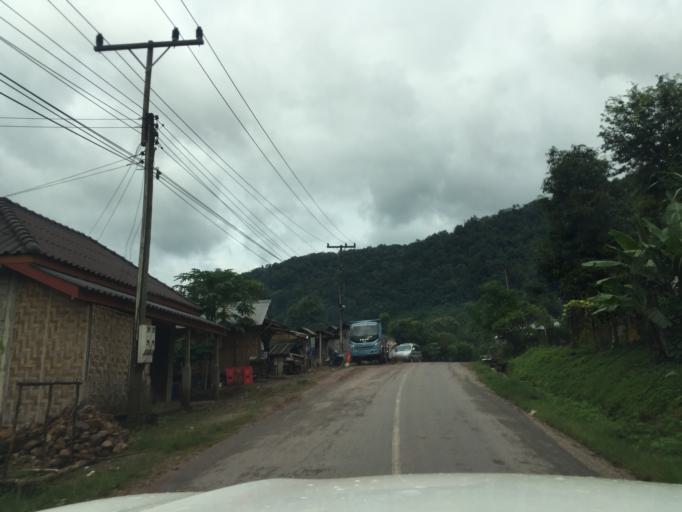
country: LA
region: Oudomxai
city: Muang La
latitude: 20.7873
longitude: 102.0748
